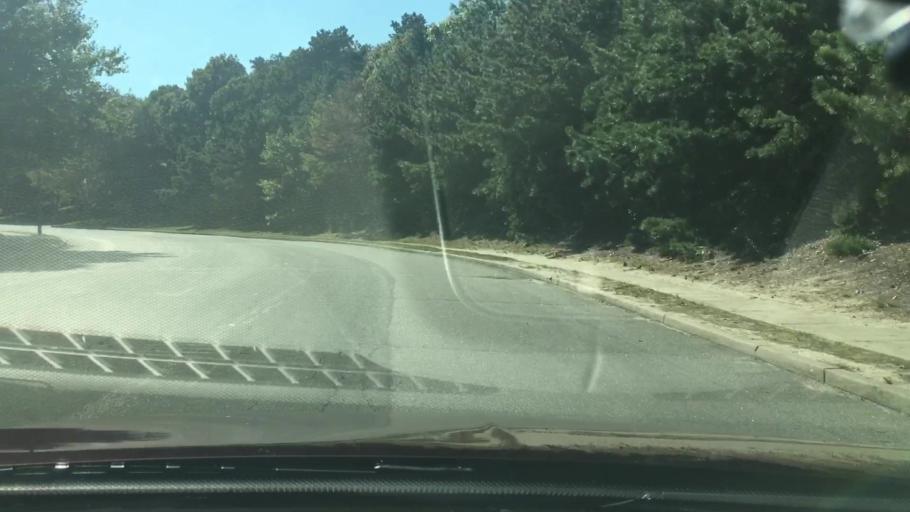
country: US
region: New York
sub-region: Suffolk County
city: Holtsville
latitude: 40.8043
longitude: -73.0394
